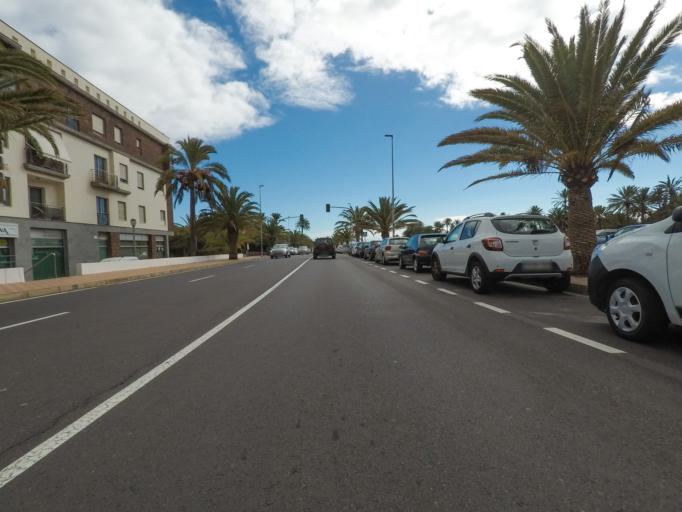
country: ES
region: Canary Islands
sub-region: Provincia de Santa Cruz de Tenerife
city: San Sebastian de la Gomera
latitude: 28.0910
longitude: -17.1134
